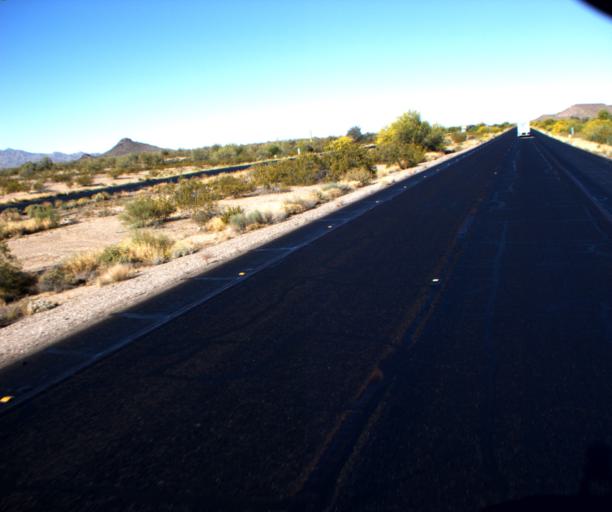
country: US
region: Arizona
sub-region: Pinal County
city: Maricopa
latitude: 32.8453
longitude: -112.2807
